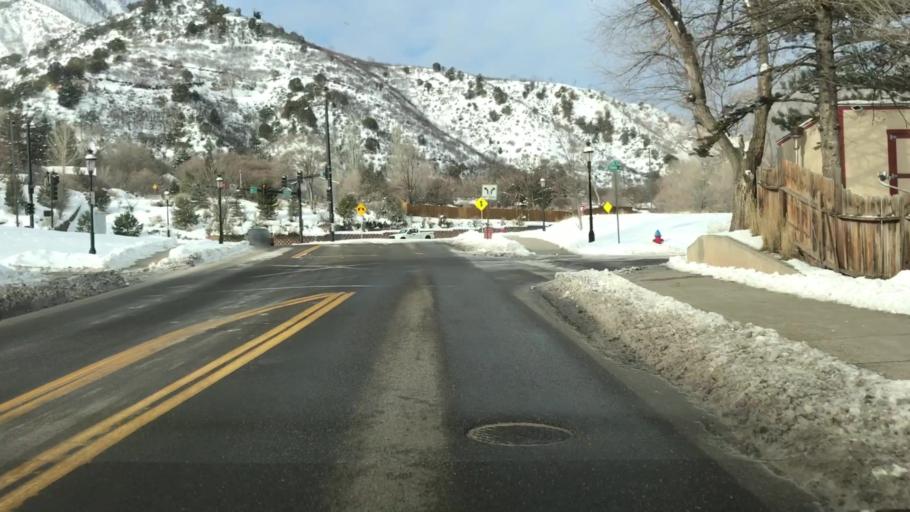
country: US
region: Colorado
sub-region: Garfield County
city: Glenwood Springs
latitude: 39.5469
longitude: -107.3311
